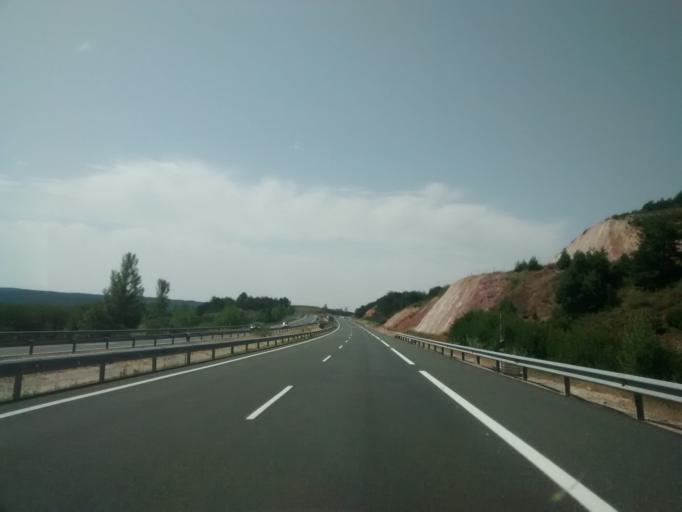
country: ES
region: Castille and Leon
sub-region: Provincia de Palencia
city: Aguilar de Campoo
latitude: 42.7366
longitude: -4.2894
